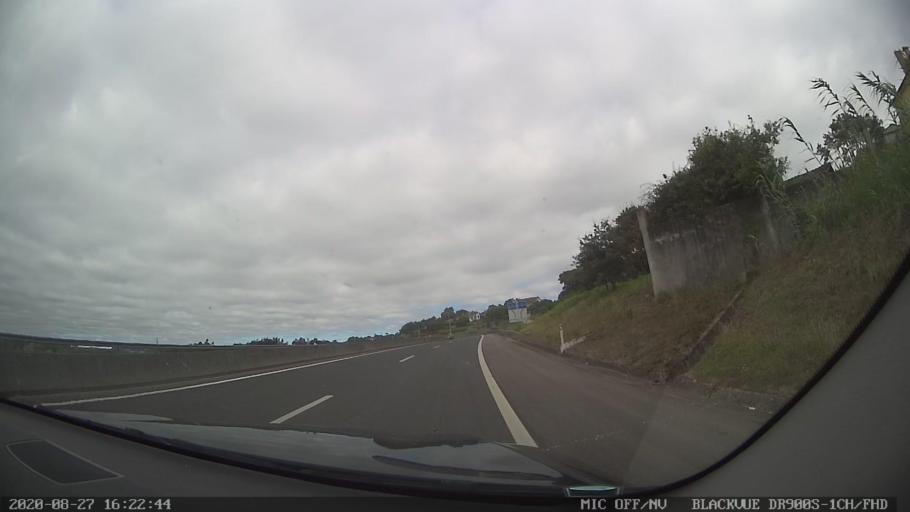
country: PT
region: Leiria
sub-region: Leiria
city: Leiria
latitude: 39.7479
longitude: -8.7803
